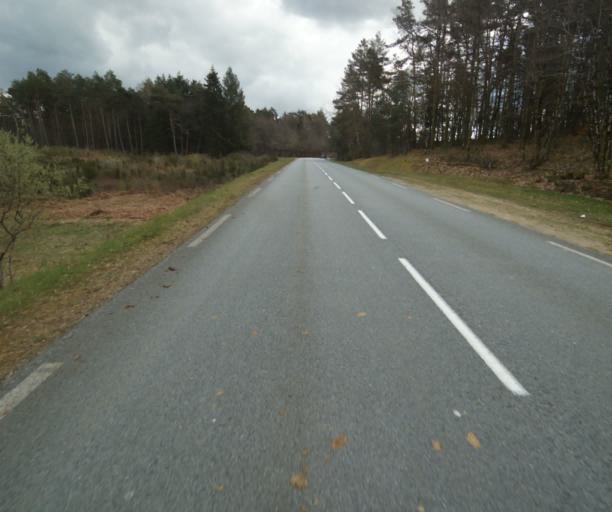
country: FR
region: Limousin
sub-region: Departement de la Correze
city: Correze
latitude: 45.2884
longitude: 1.9020
